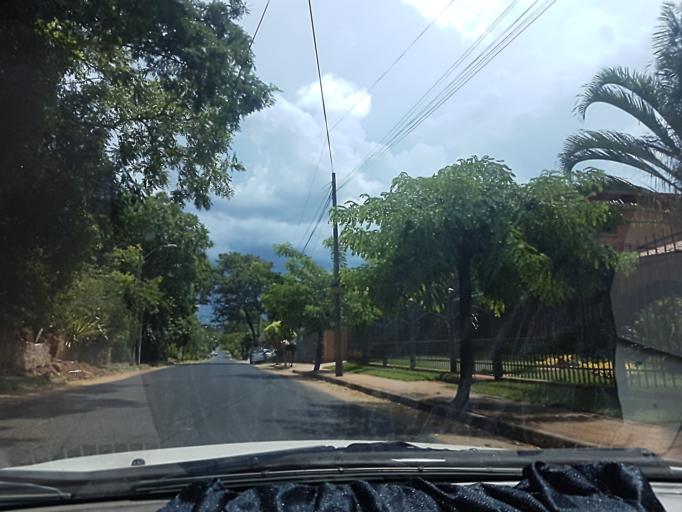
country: PY
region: Central
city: Fernando de la Mora
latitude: -25.2637
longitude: -57.5593
